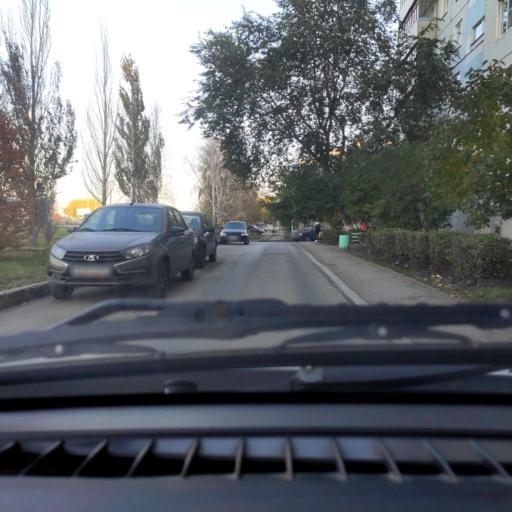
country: RU
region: Samara
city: Tol'yatti
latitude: 53.5470
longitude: 49.3532
